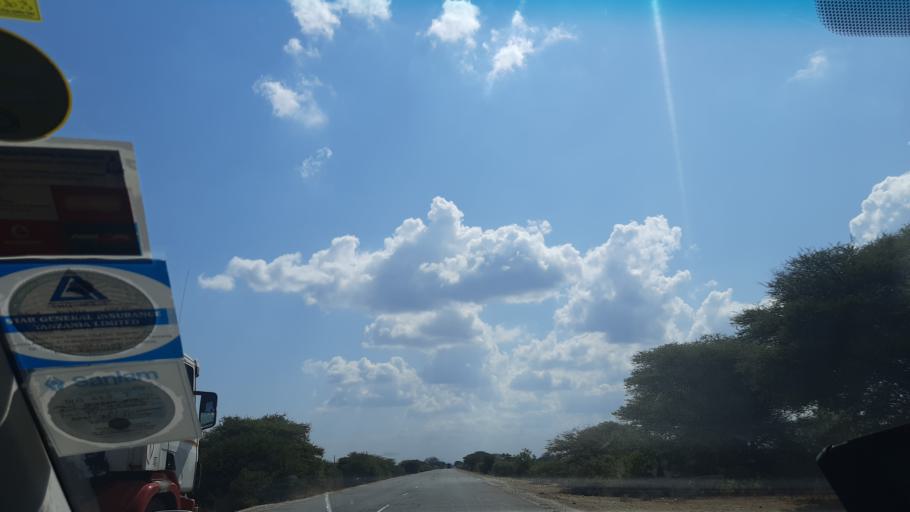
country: TZ
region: Singida
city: Kintinku
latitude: -5.9369
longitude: 35.2889
